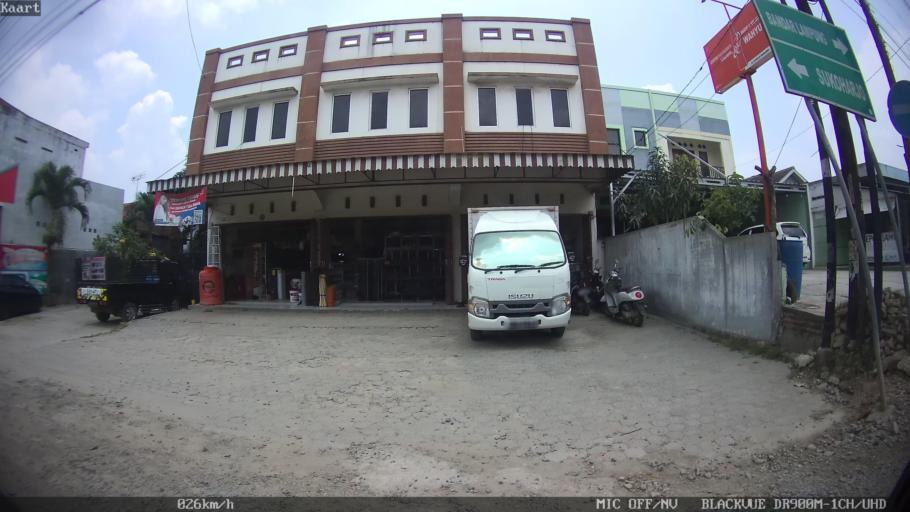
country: ID
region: Lampung
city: Pringsewu
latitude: -5.3498
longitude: 104.9760
